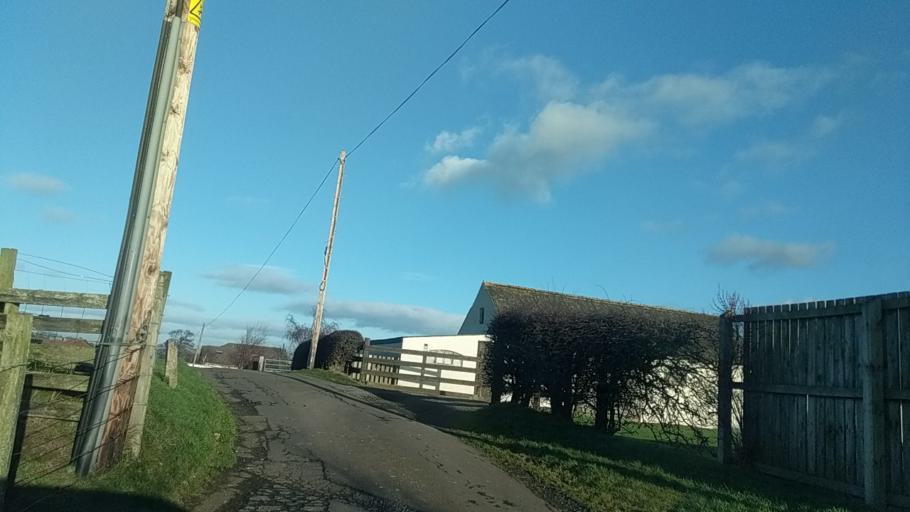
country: GB
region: Scotland
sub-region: West Lothian
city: Linlithgow
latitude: 55.9922
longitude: -3.5426
